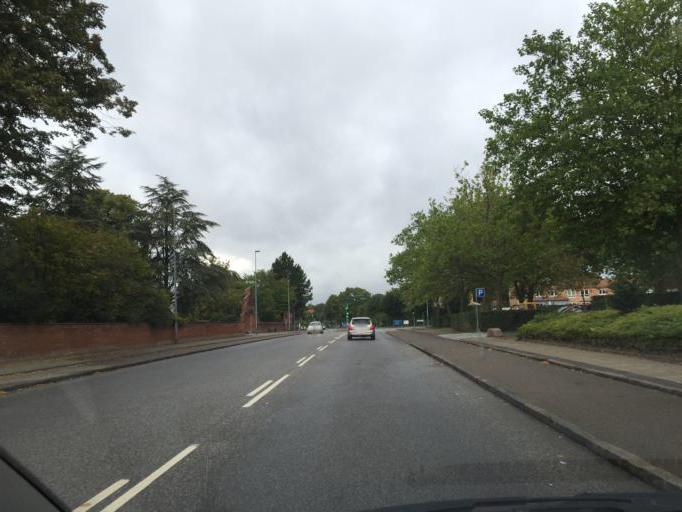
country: DK
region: Capital Region
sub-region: Gladsaxe Municipality
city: Buddinge
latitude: 55.7389
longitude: 12.4742
